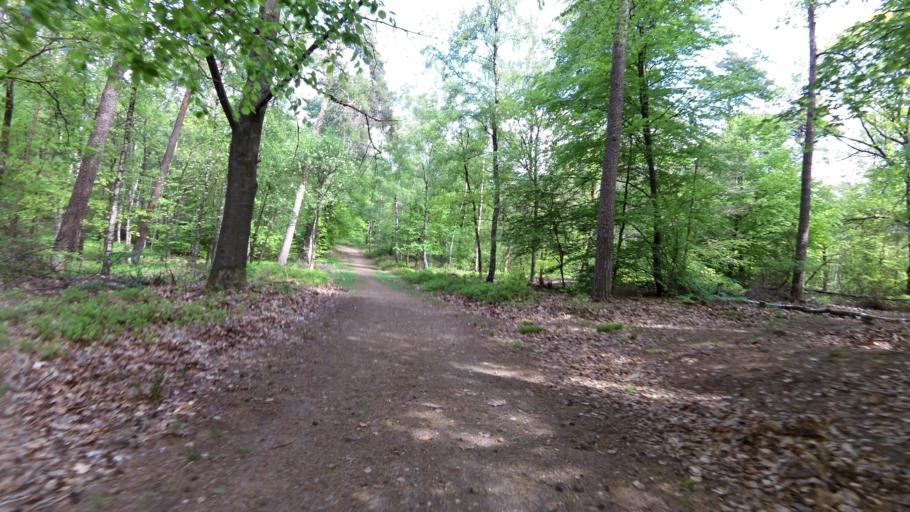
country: NL
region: Gelderland
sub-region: Gemeente Rozendaal
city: Rozendaal
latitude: 52.0152
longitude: 5.9742
